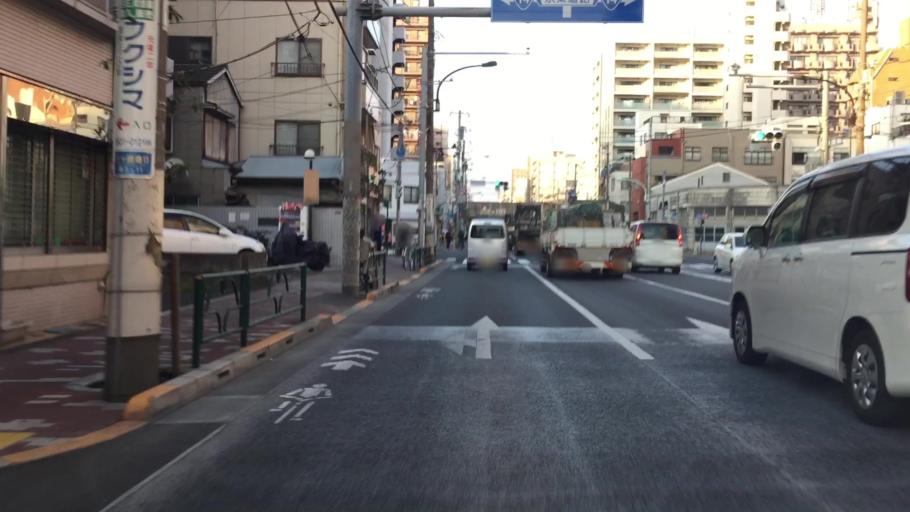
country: JP
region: Tokyo
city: Urayasu
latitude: 35.6945
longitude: 139.8055
